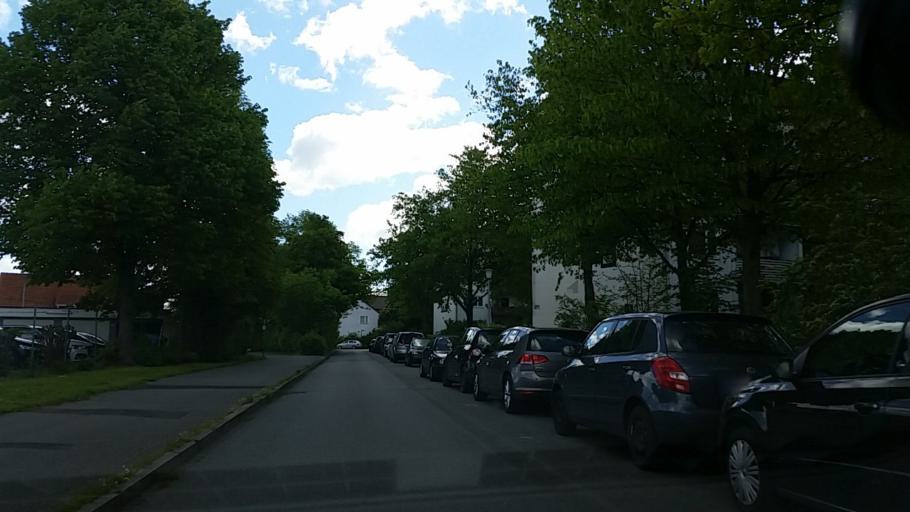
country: DE
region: Lower Saxony
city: Wolfsburg
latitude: 52.4243
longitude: 10.8007
